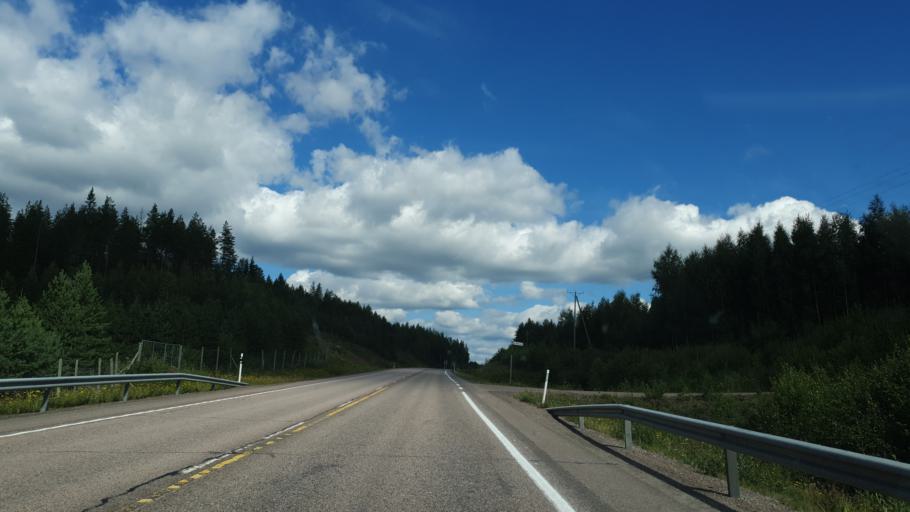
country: FI
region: Central Finland
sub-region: Jaemsae
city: Jaemsae
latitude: 61.8029
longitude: 24.9703
